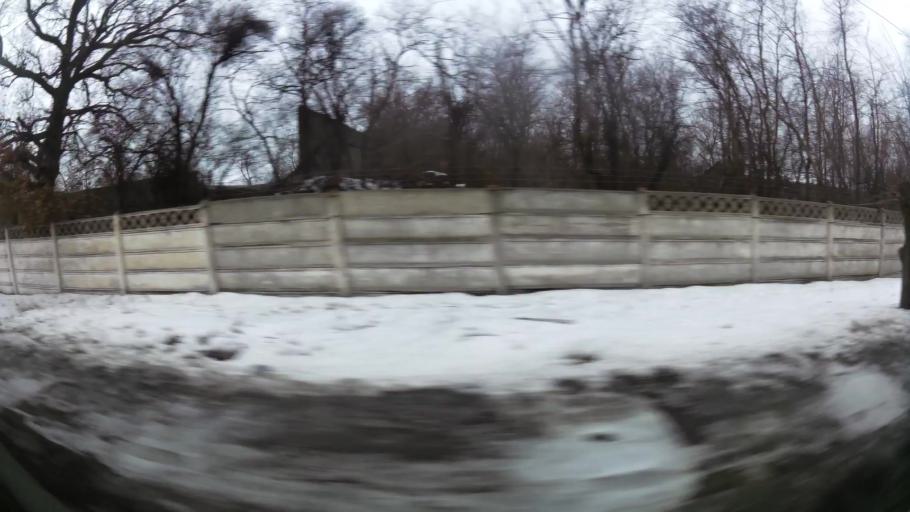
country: RO
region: Ilfov
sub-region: Comuna Clinceni
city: Olteni
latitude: 44.4178
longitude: 25.9699
